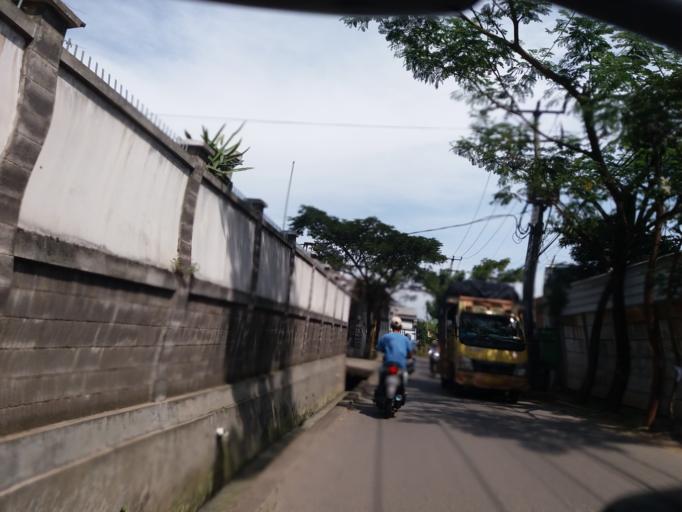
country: ID
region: West Java
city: Margahayukencana
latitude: -6.9451
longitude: 107.5680
